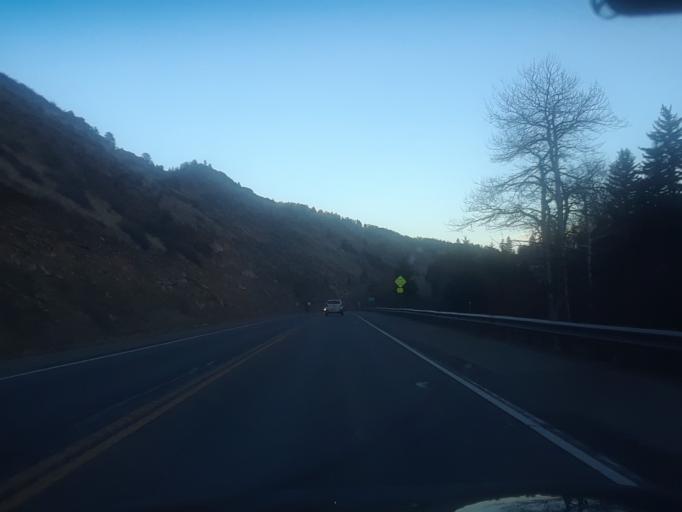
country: US
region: Colorado
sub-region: Clear Creek County
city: Georgetown
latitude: 39.4607
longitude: -105.6843
